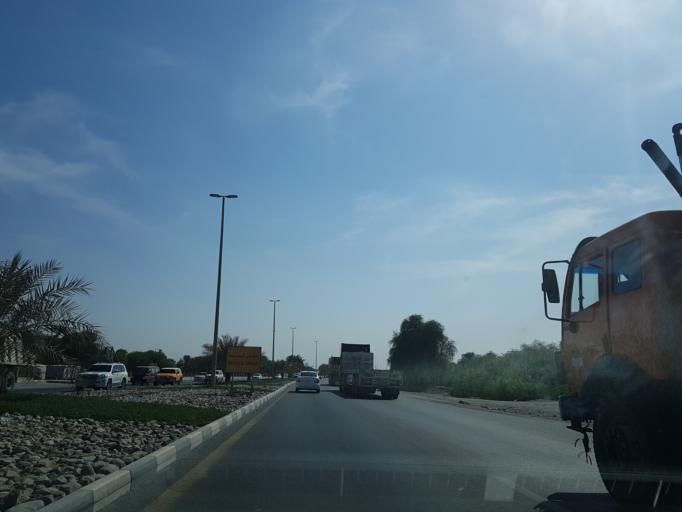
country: AE
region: Ra's al Khaymah
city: Ras al-Khaimah
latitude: 25.7067
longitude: 55.9697
